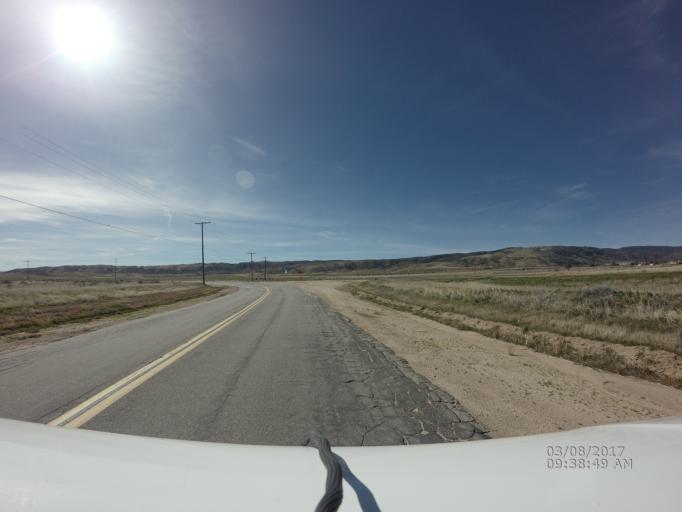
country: US
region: California
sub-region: Los Angeles County
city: Green Valley
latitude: 34.7400
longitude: -118.4664
